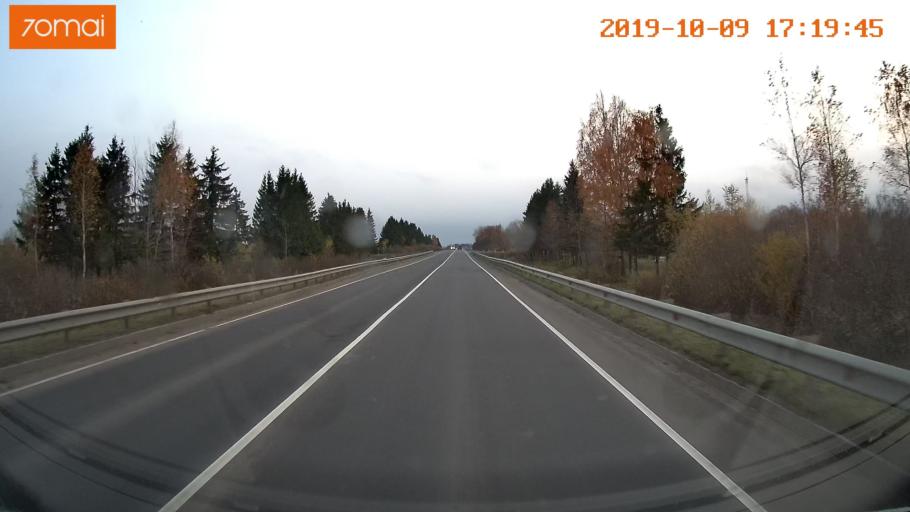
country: RU
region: Ivanovo
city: Furmanov
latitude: 57.2423
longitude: 41.1491
